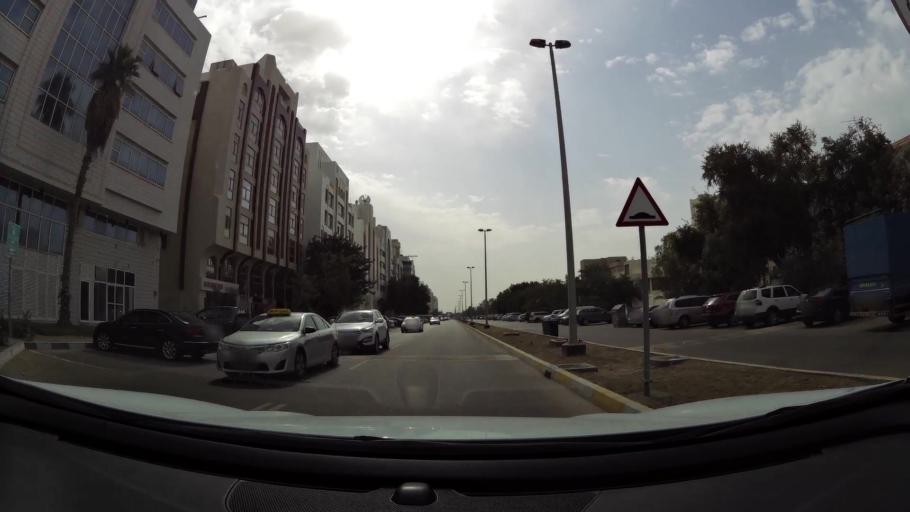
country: AE
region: Abu Dhabi
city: Abu Dhabi
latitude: 24.4537
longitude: 54.3848
